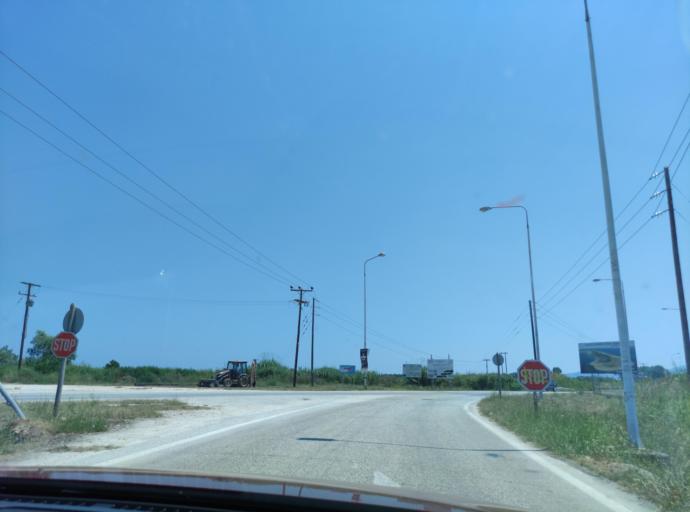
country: GR
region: East Macedonia and Thrace
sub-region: Nomos Kavalas
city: Keramoti
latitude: 40.8682
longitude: 24.7048
